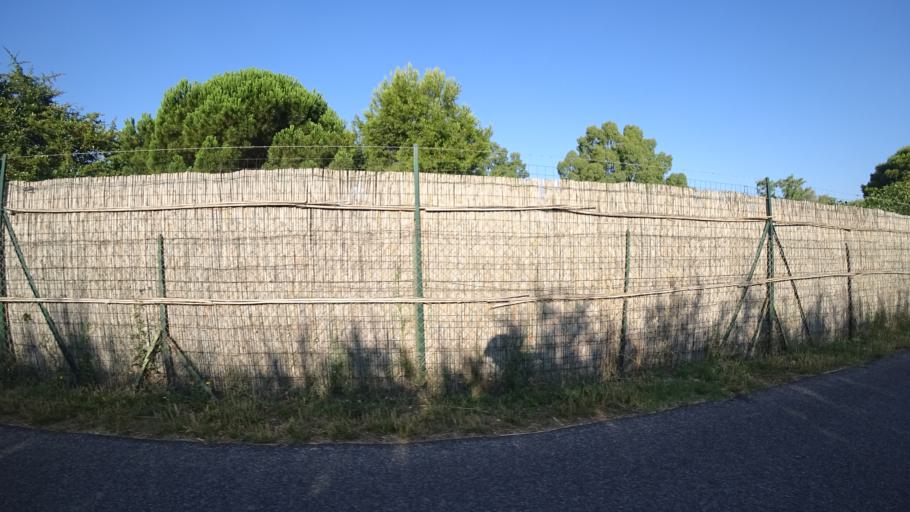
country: FR
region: Languedoc-Roussillon
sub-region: Departement des Pyrenees-Orientales
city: Sainte-Marie-Plage
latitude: 42.7283
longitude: 3.0283
